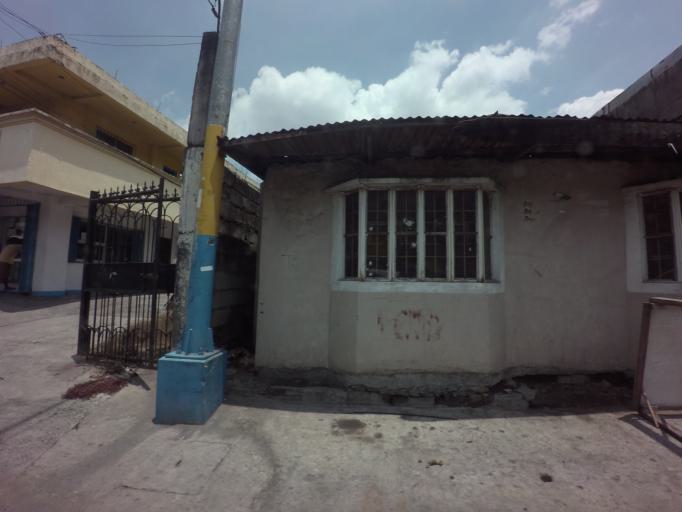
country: PH
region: Calabarzon
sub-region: Province of Laguna
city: San Pedro
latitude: 14.3874
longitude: 121.0500
